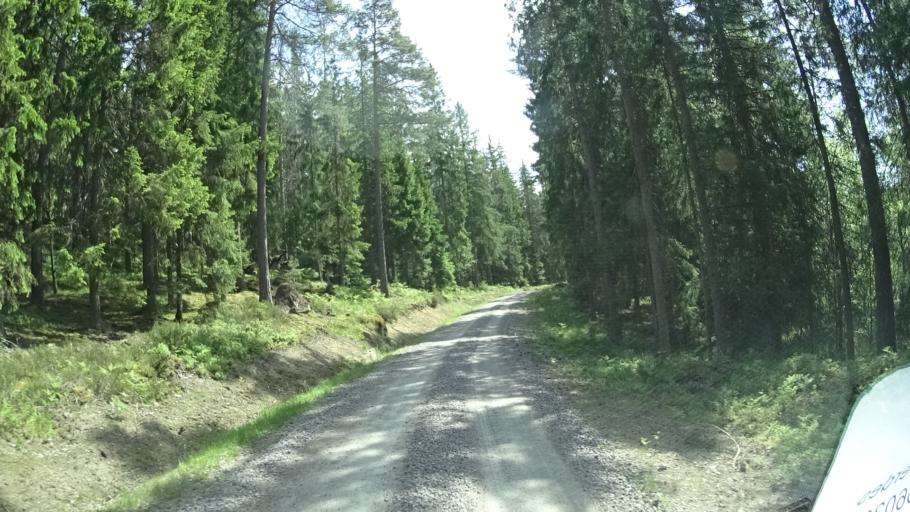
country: SE
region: OEstergoetland
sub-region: Norrkopings Kommun
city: Svartinge
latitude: 58.7779
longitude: 15.9299
